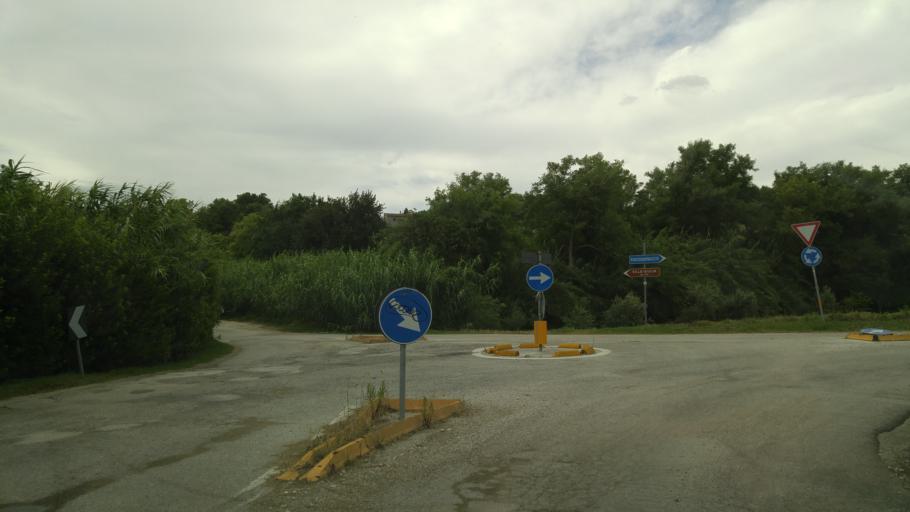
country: IT
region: The Marches
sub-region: Provincia di Pesaro e Urbino
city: Fenile
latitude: 43.8659
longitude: 12.9818
